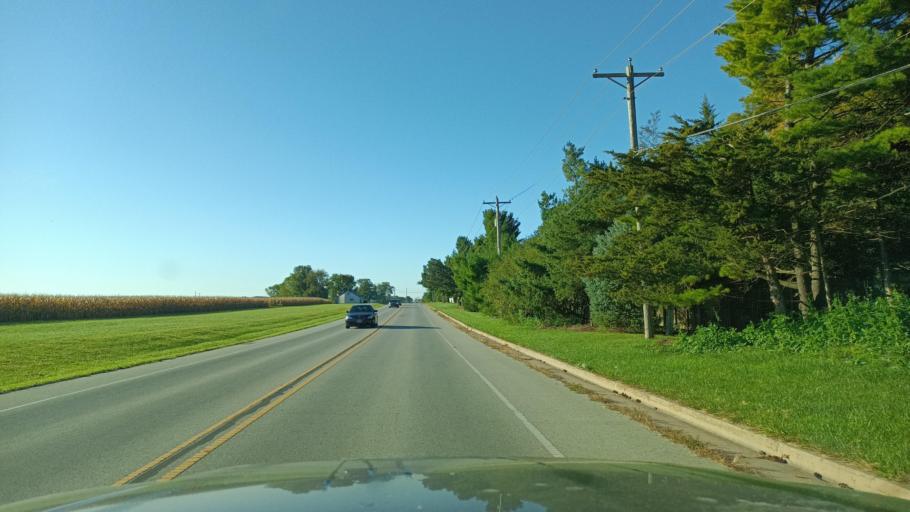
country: US
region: Illinois
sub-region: Champaign County
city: Savoy
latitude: 40.0638
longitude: -88.2384
